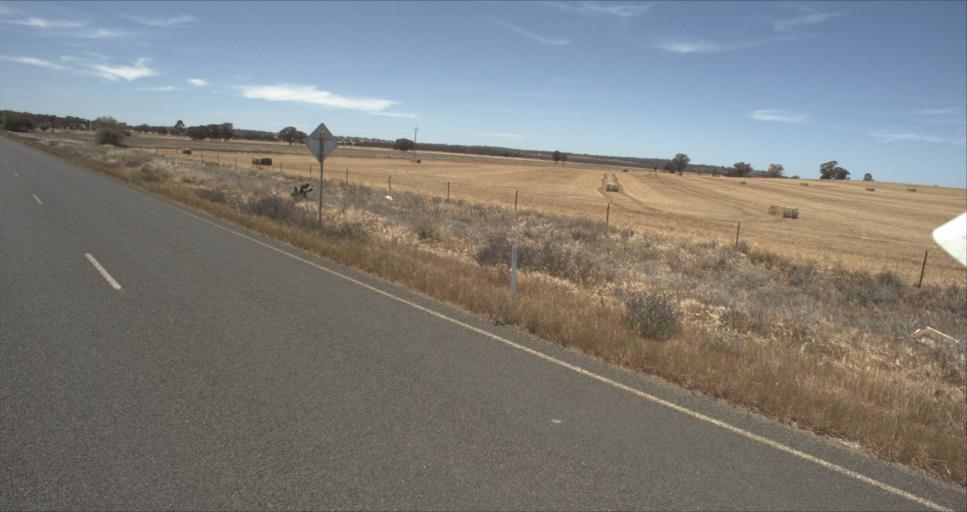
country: AU
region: New South Wales
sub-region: Leeton
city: Leeton
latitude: -34.6523
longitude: 146.4635
